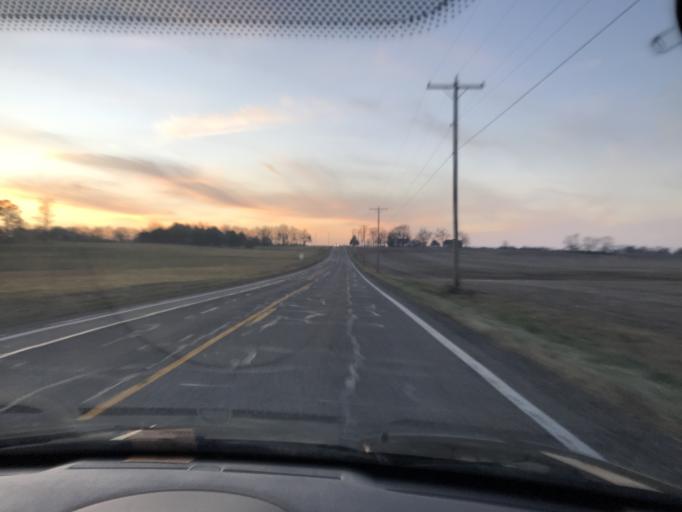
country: US
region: Ohio
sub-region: Champaign County
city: Urbana
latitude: 40.1083
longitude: -83.6975
